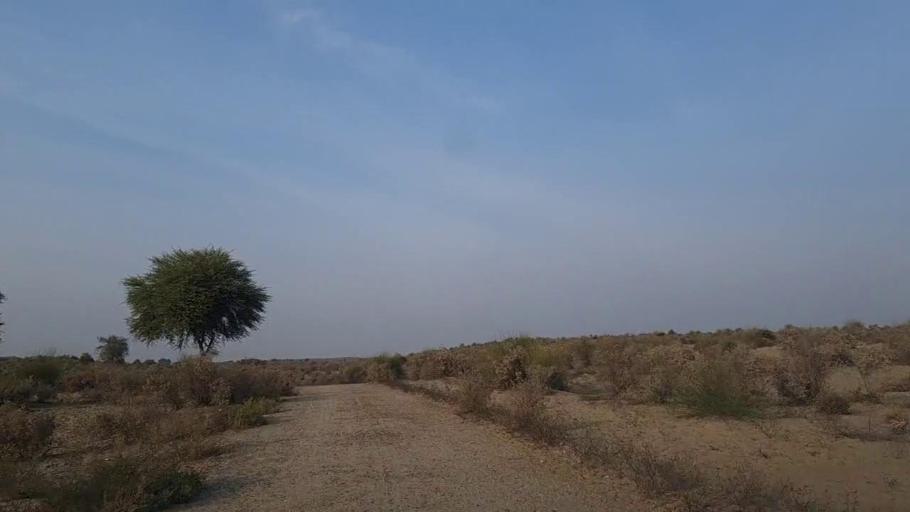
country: PK
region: Sindh
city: Jam Sahib
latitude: 26.4261
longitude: 68.6037
